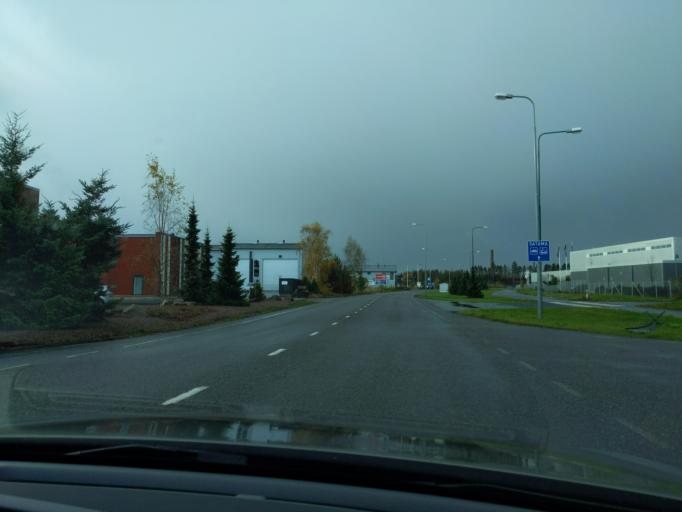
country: FI
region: Varsinais-Suomi
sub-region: Turku
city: Naantali
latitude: 60.4719
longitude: 22.0627
